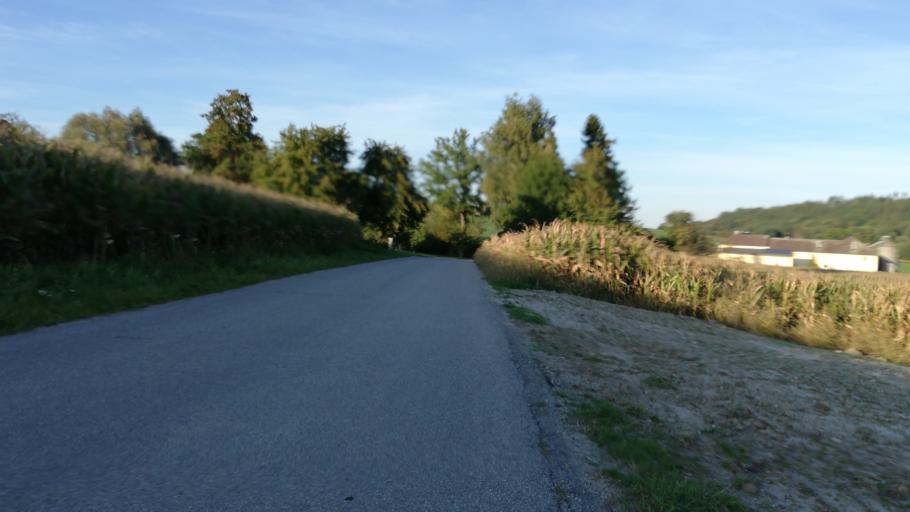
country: AT
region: Upper Austria
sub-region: Wels-Land
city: Pennewang
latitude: 48.1717
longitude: 13.8867
